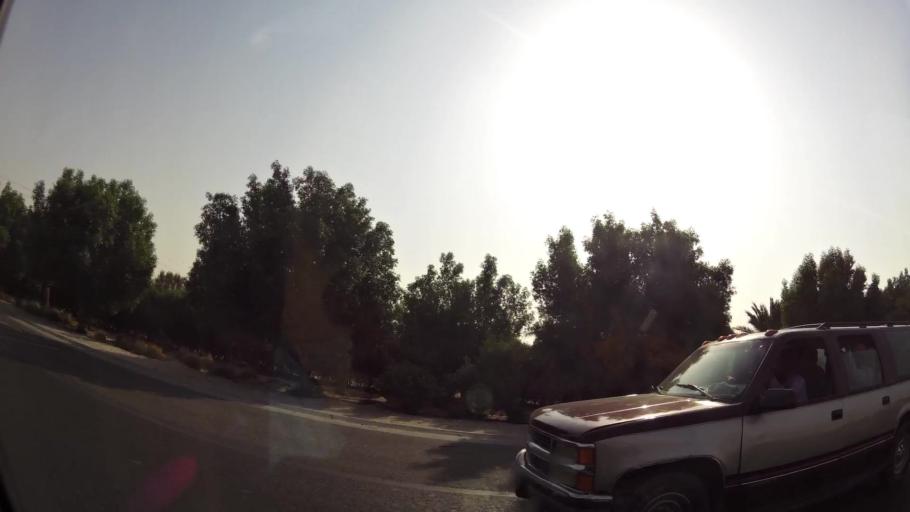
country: KW
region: Muhafazat al Jahra'
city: Al Jahra'
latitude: 29.3183
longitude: 47.7623
